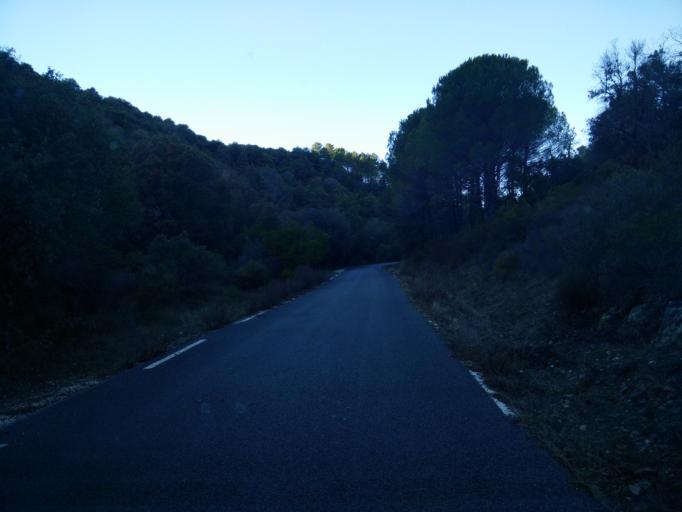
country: FR
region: Provence-Alpes-Cote d'Azur
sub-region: Departement du Var
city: Collobrieres
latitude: 43.2346
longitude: 6.3616
